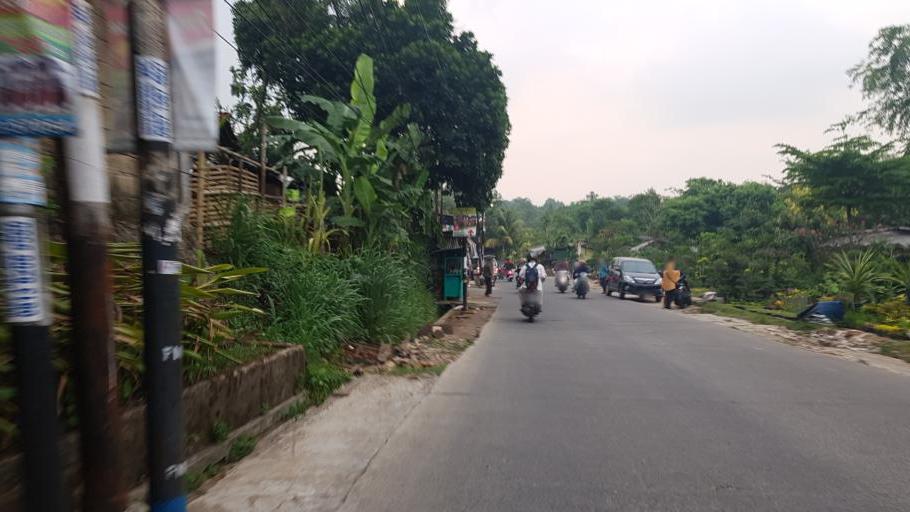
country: ID
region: West Java
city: Depok
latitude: -6.3694
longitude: 106.8119
